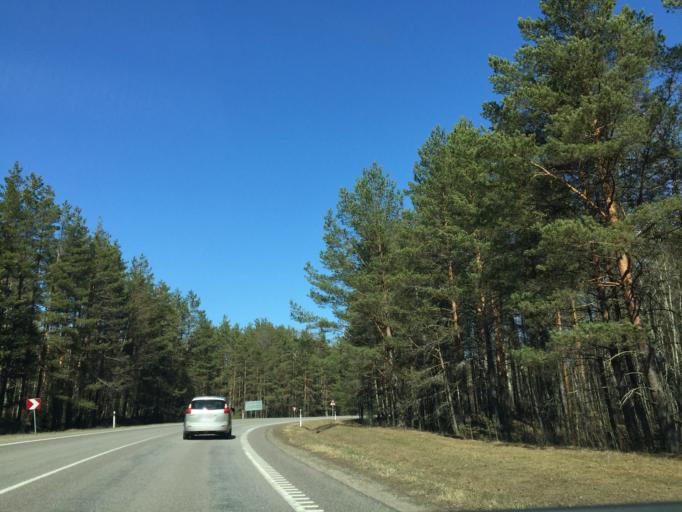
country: EE
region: Jogevamaa
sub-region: Mustvee linn
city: Mustvee
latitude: 58.9906
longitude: 27.1740
